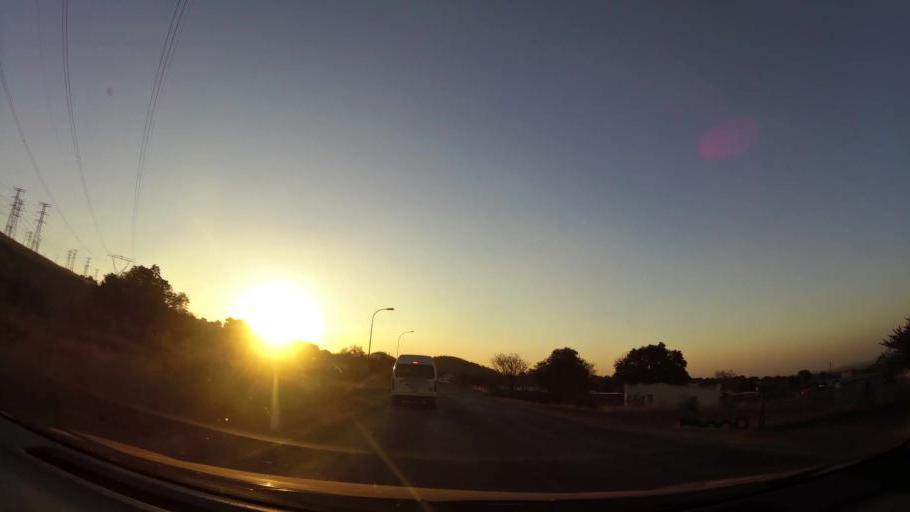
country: ZA
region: North-West
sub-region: Bojanala Platinum District Municipality
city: Rustenburg
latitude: -25.6308
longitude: 27.2014
